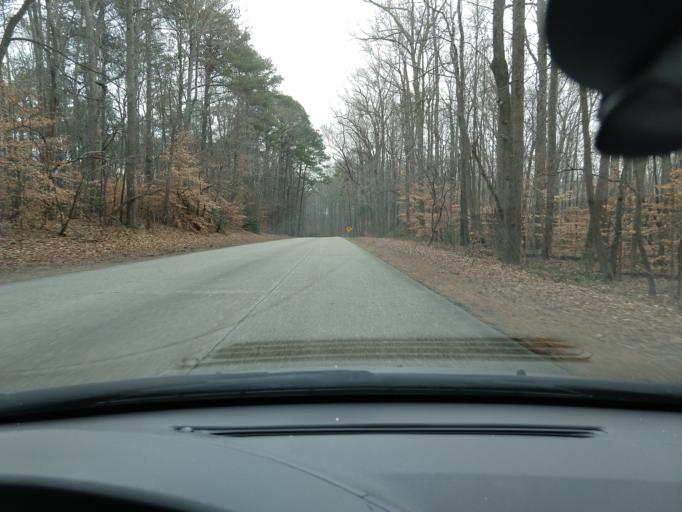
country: US
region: Virginia
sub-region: City of Williamsburg
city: Williamsburg
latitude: 37.2762
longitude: -76.6157
